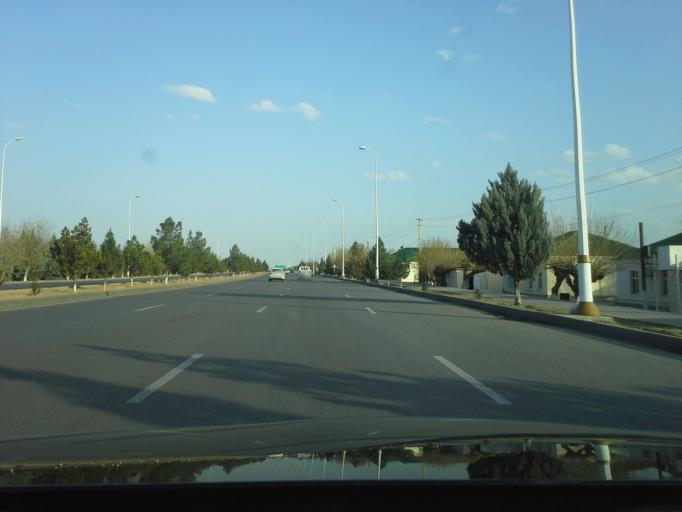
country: TM
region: Ahal
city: Abadan
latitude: 38.0295
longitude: 58.2323
